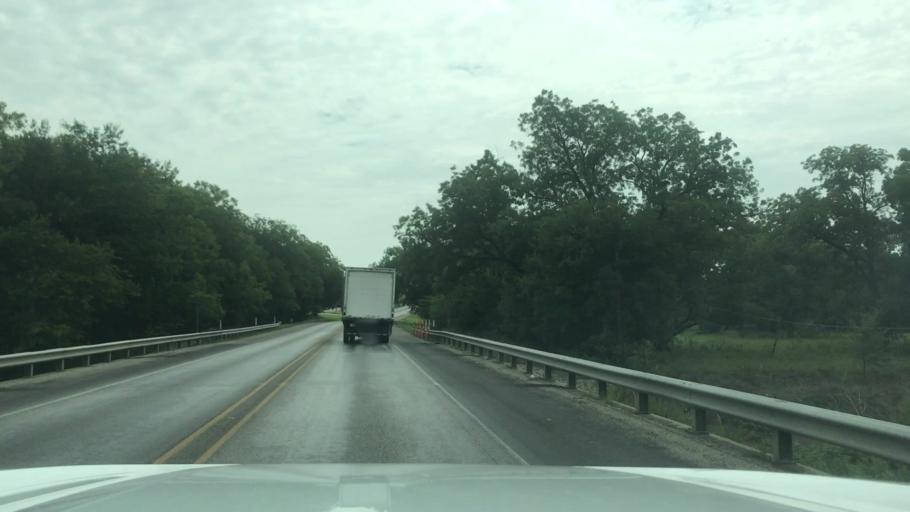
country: US
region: Texas
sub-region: Comanche County
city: De Leon
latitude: 32.1030
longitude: -98.4814
